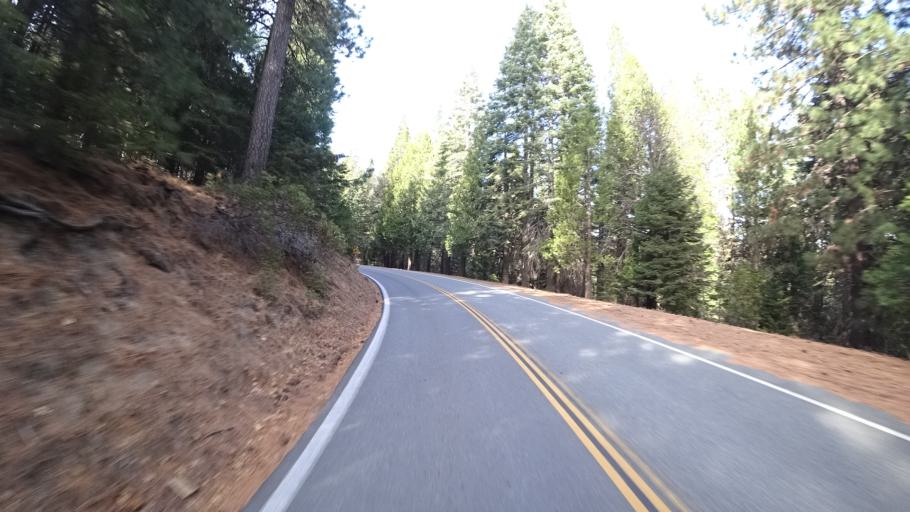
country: US
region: California
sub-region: Siskiyou County
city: Weed
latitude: 41.3813
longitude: -122.3878
